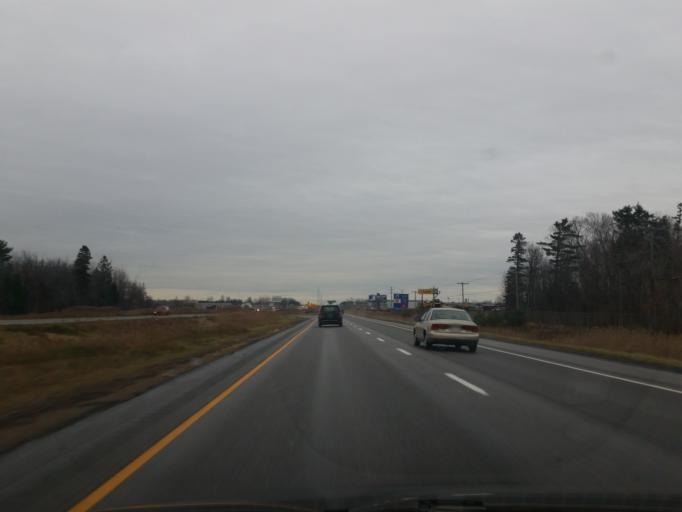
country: CA
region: Quebec
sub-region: Capitale-Nationale
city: Saint-Augustin-de-Desmaures
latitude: 46.7604
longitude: -71.4453
